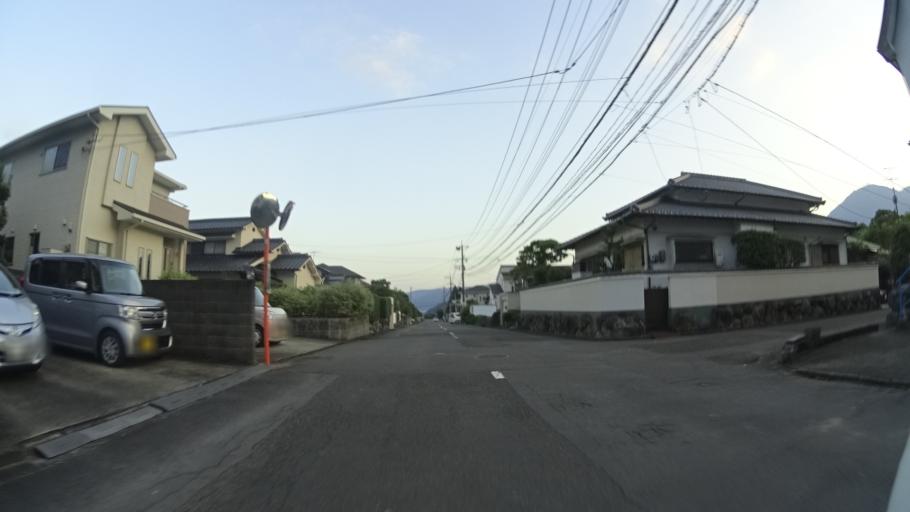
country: JP
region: Oita
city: Beppu
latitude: 33.3185
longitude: 131.4844
